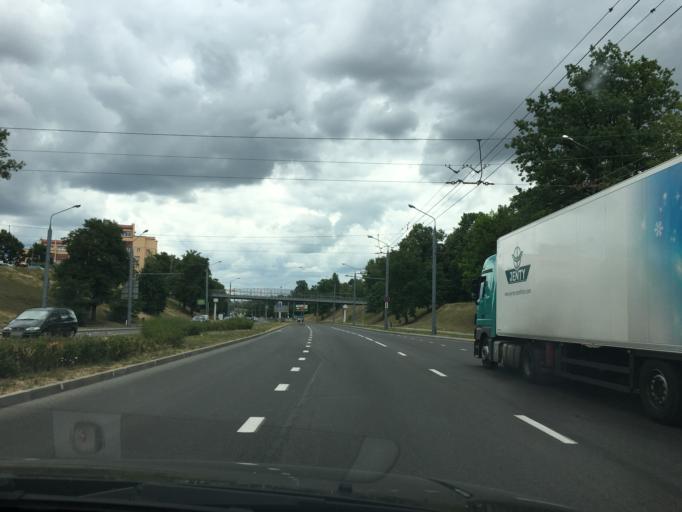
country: BY
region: Grodnenskaya
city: Hrodna
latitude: 53.6546
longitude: 23.8565
